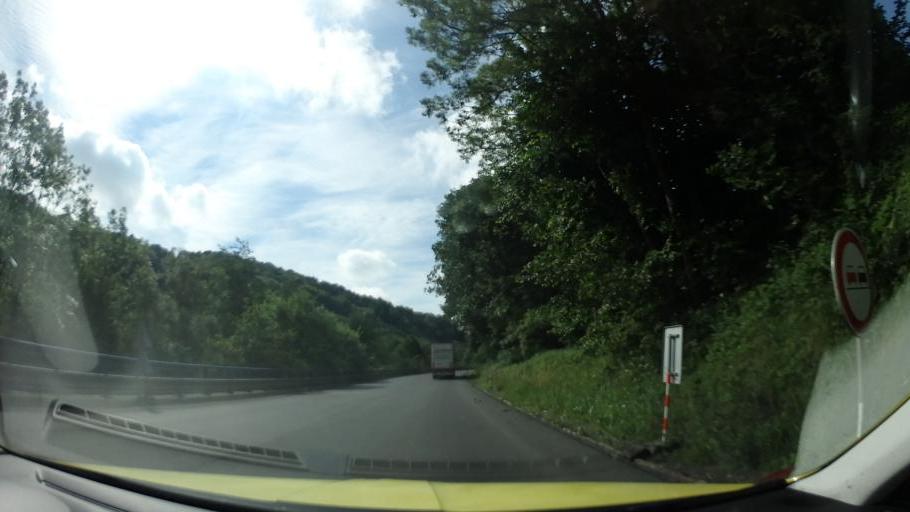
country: CZ
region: Moravskoslezsky
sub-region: Okres Novy Jicin
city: Novy Jicin
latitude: 49.5707
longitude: 18.0242
